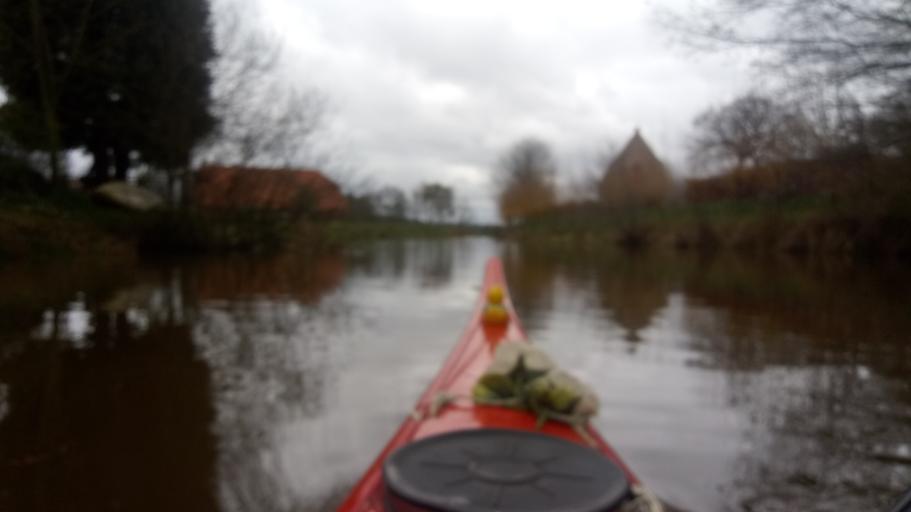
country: NL
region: Groningen
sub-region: Gemeente Vlagtwedde
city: Sellingen
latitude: 52.9748
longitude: 7.1500
